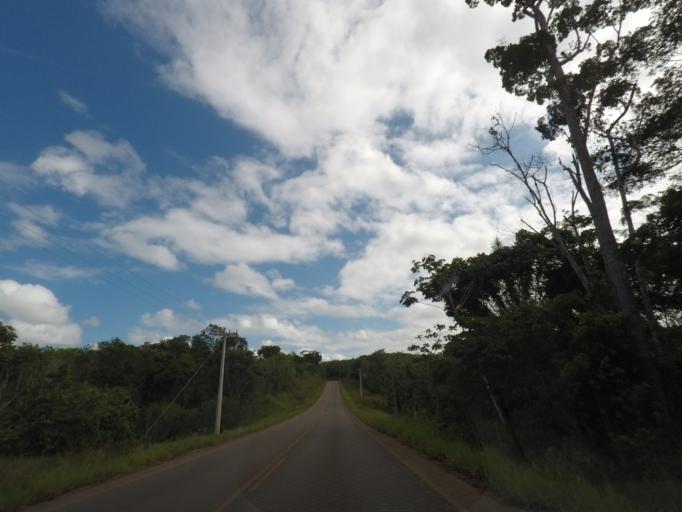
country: BR
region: Bahia
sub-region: Itacare
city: Itacare
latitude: -14.2217
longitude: -39.0980
